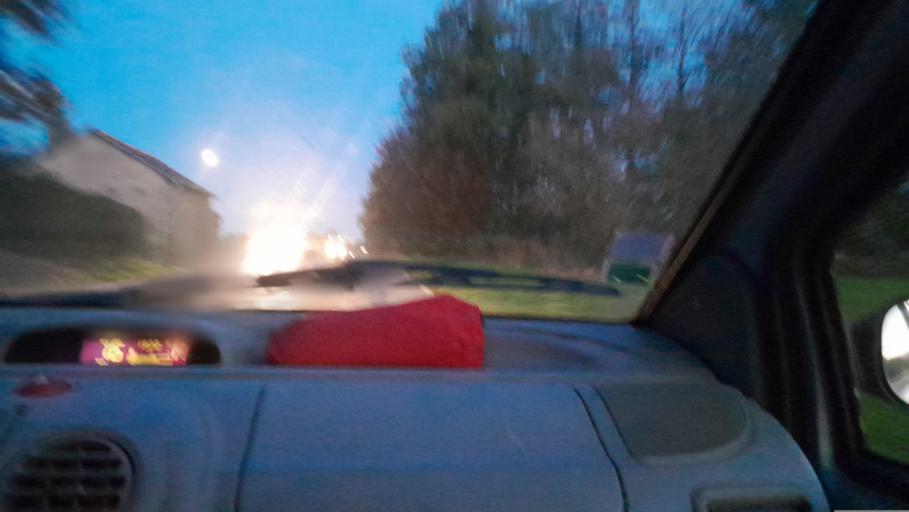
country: FR
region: Brittany
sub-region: Departement d'Ille-et-Vilaine
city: La Guerche-de-Bretagne
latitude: 47.9015
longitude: -1.1515
